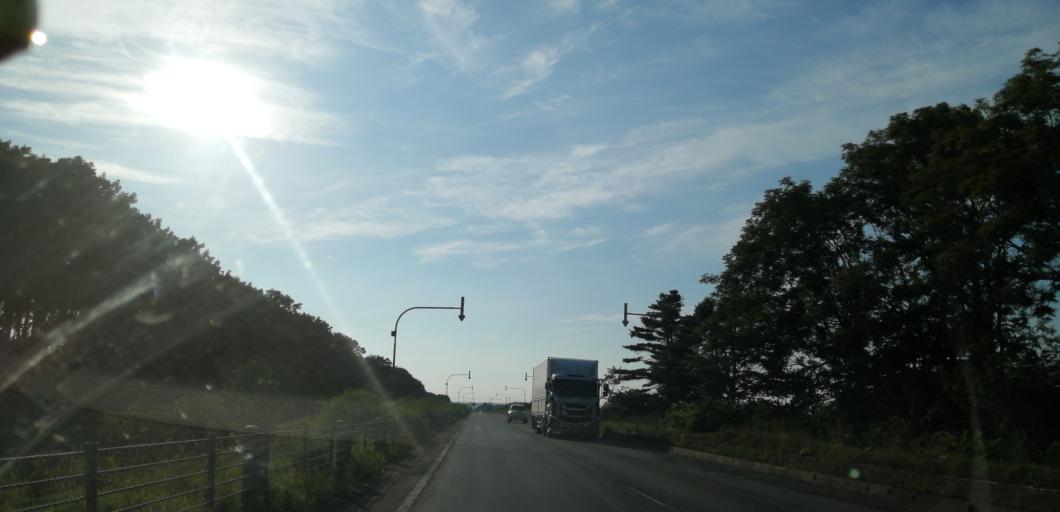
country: JP
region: Hokkaido
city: Kitahiroshima
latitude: 42.9786
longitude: 141.6399
